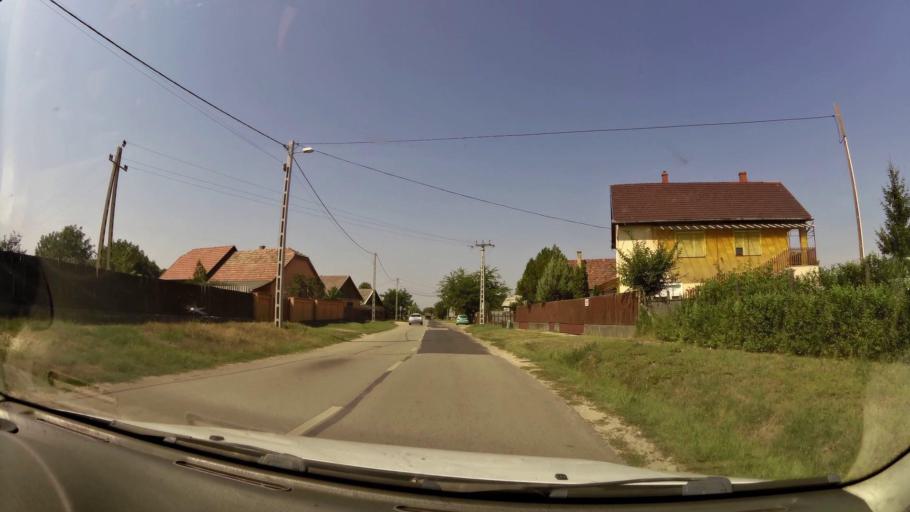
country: HU
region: Pest
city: Tapioszentmarton
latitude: 47.3435
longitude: 19.7752
